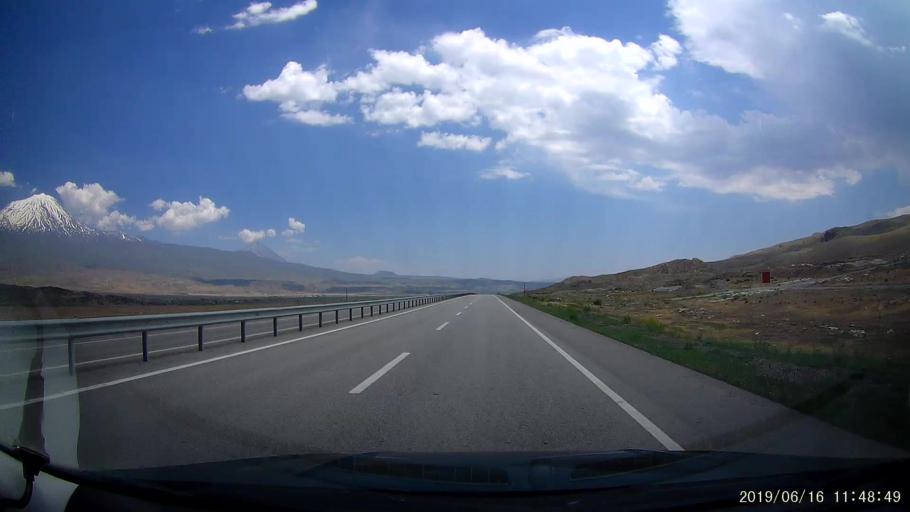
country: TR
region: Agri
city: Dogubayazit
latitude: 39.5578
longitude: 44.1511
